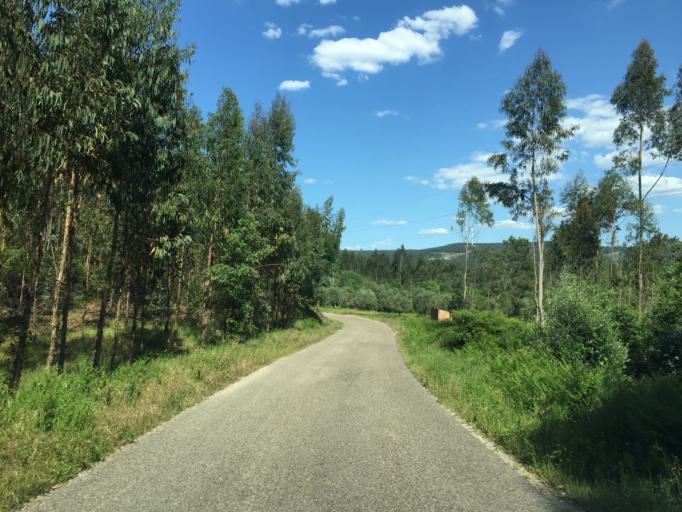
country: PT
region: Leiria
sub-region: Alvaiazere
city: Alvaiazere
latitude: 39.8461
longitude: -8.3656
